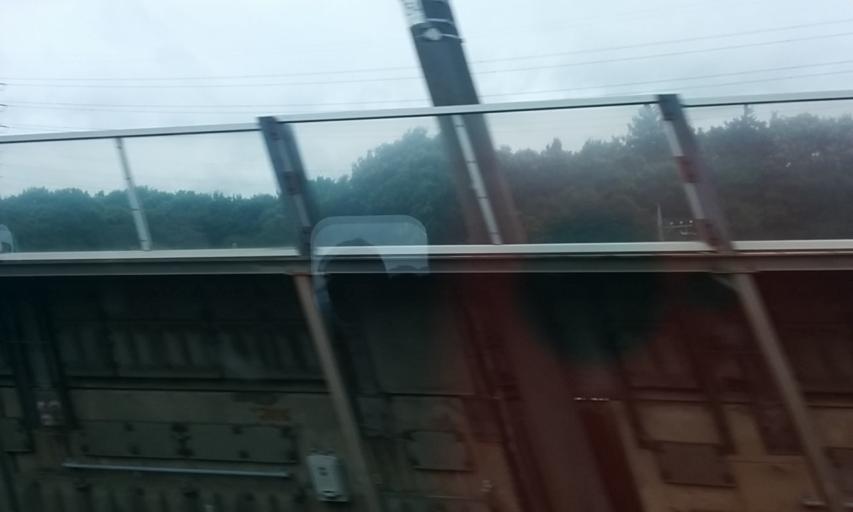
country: JP
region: Tochigi
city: Oyama
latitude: 36.2761
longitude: 139.7773
